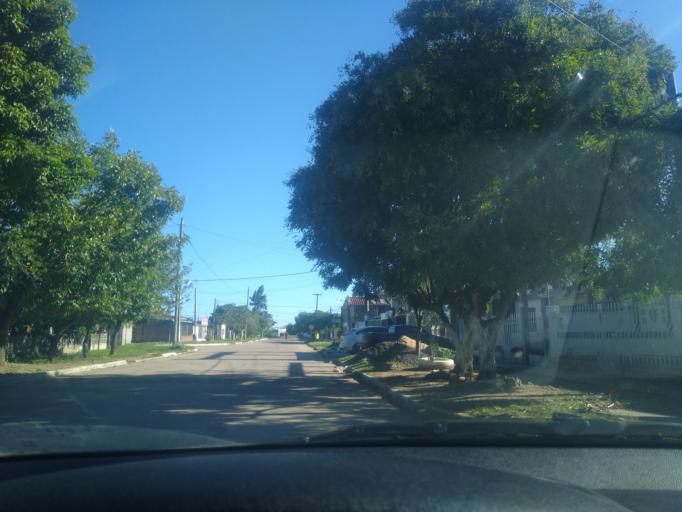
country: AR
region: Chaco
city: Puerto Vilelas
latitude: -27.5175
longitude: -58.9437
